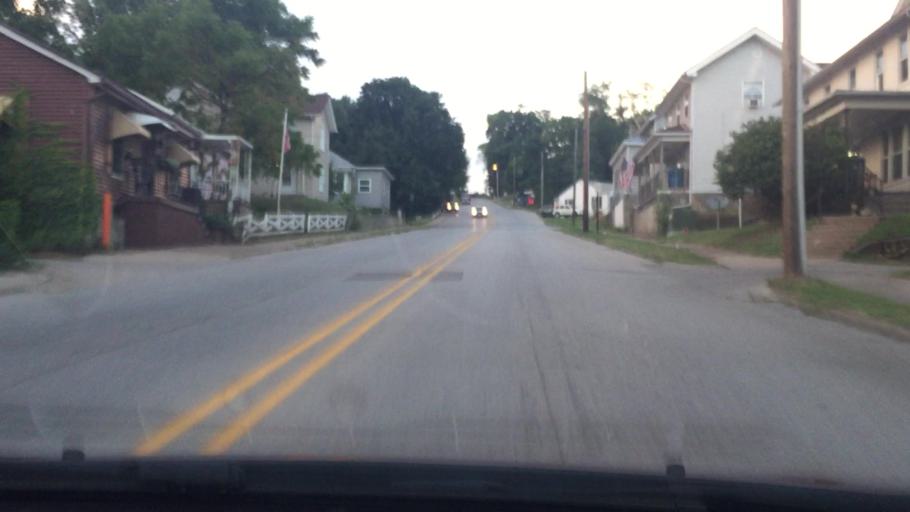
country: US
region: Iowa
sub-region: Muscatine County
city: Muscatine
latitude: 41.4157
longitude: -91.0589
